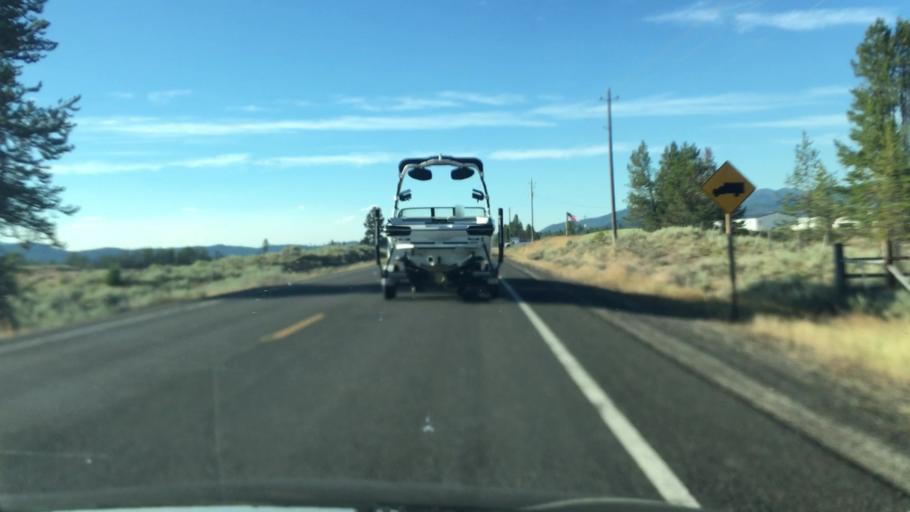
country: US
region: Idaho
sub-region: Valley County
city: Cascade
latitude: 44.4729
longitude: -115.9992
